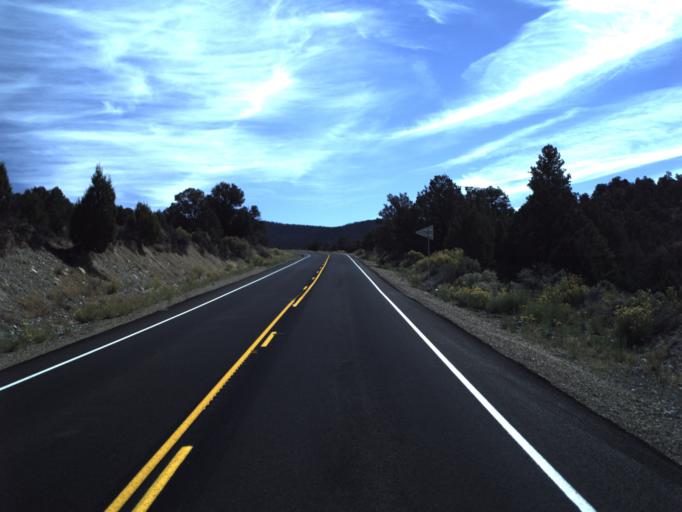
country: US
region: Utah
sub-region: Garfield County
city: Panguitch
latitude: 37.6162
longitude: -111.8895
